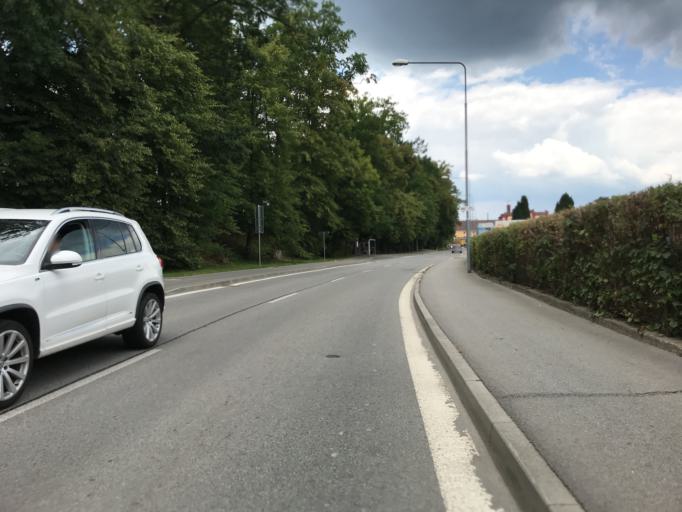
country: CZ
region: Jihocesky
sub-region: Okres Jindrichuv Hradec
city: Trebon
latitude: 48.9990
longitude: 14.7733
